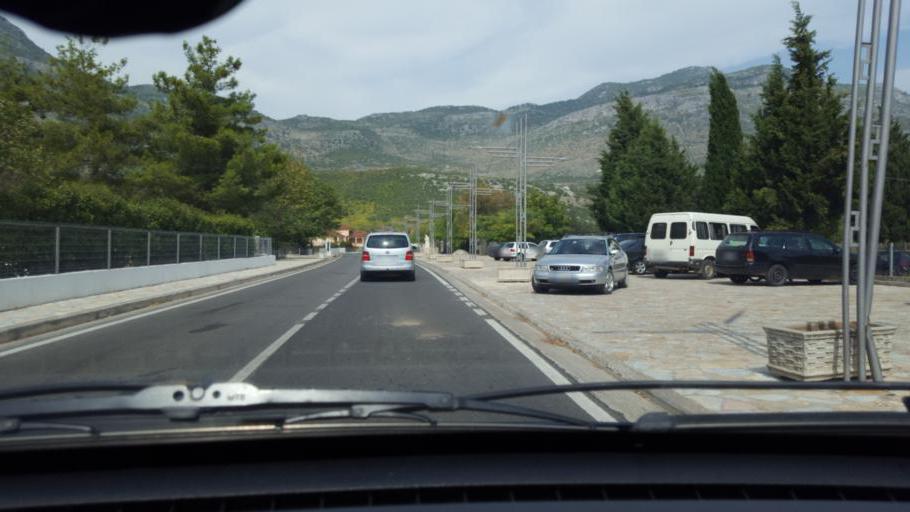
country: AL
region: Shkoder
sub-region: Rrethi i Malesia e Madhe
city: Hot
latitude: 42.3599
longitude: 19.4430
